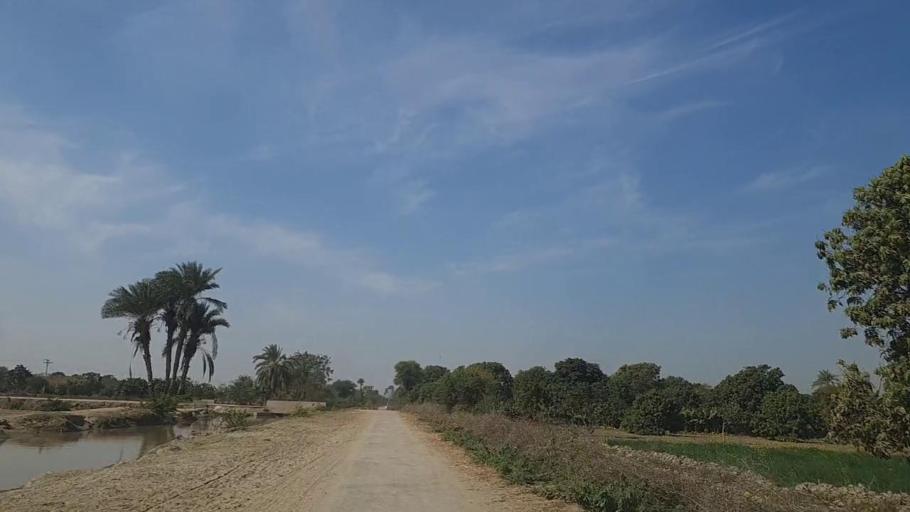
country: PK
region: Sindh
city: Mirpur Khas
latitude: 25.4683
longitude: 68.9632
